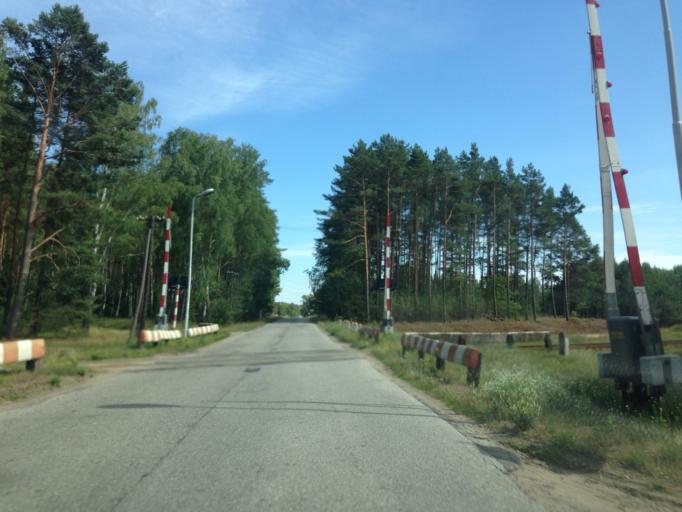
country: PL
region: Pomeranian Voivodeship
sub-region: Powiat starogardzki
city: Szlachta
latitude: 53.7443
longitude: 18.1126
